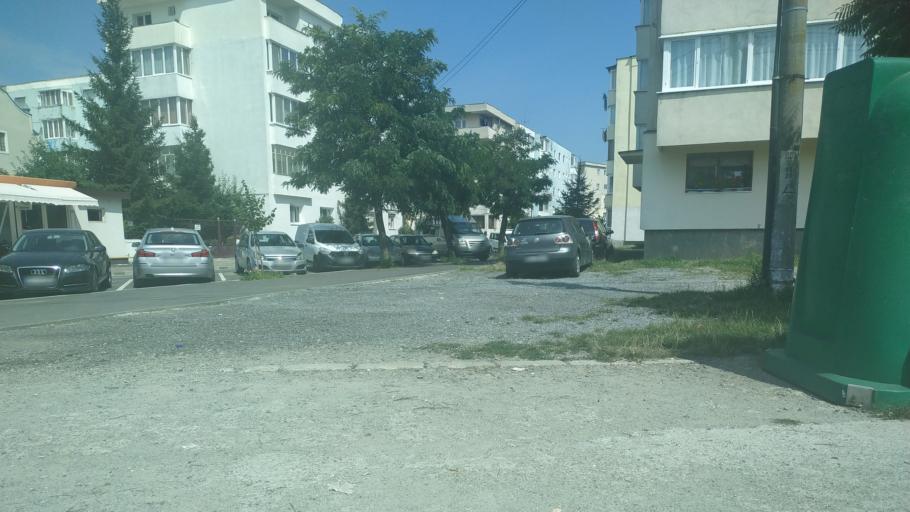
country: RO
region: Brasov
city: Fogarasch
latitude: 45.8408
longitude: 24.9663
